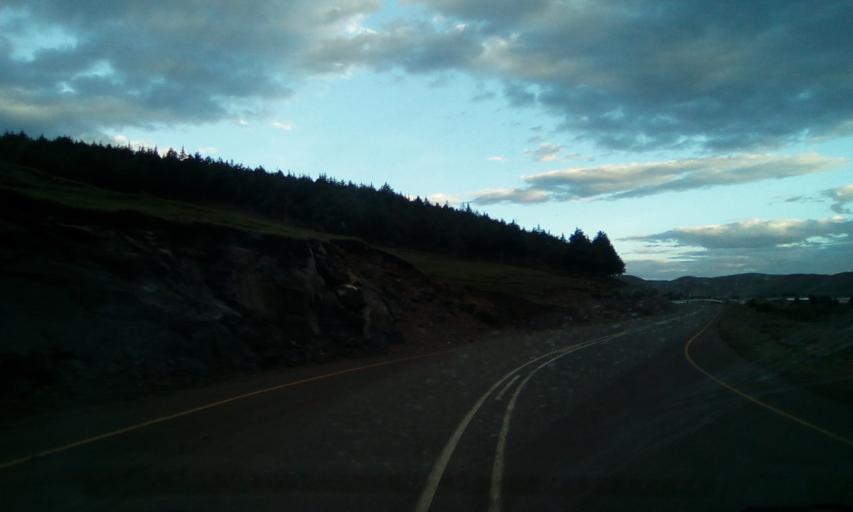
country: LS
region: Maseru
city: Nako
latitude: -29.8262
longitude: 28.0373
